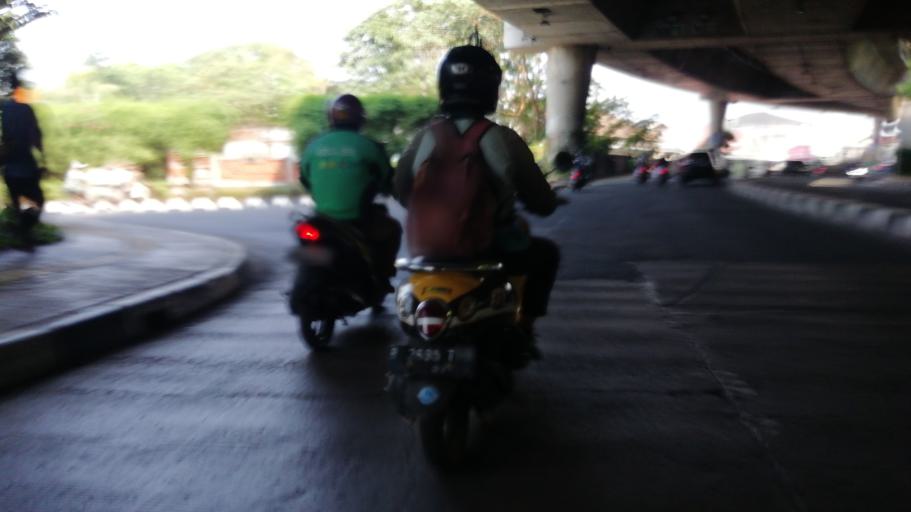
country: ID
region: Jakarta Raya
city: Jakarta
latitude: -6.2495
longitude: 106.8089
